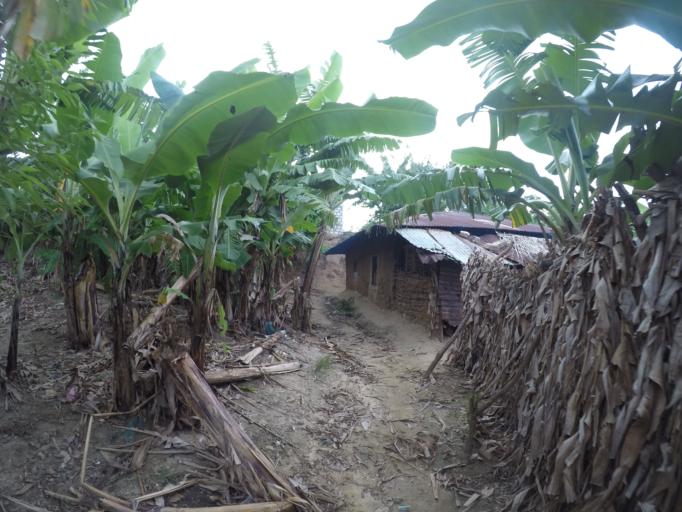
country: TZ
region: Pemba South
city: Chake Chake
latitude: -5.2521
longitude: 39.7760
